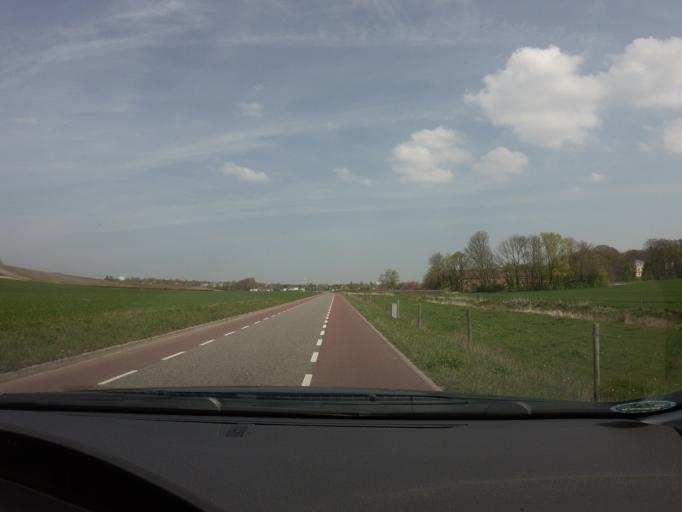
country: NL
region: Limburg
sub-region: Gemeente Maastricht
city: Maastricht
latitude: 50.8264
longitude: 5.6688
